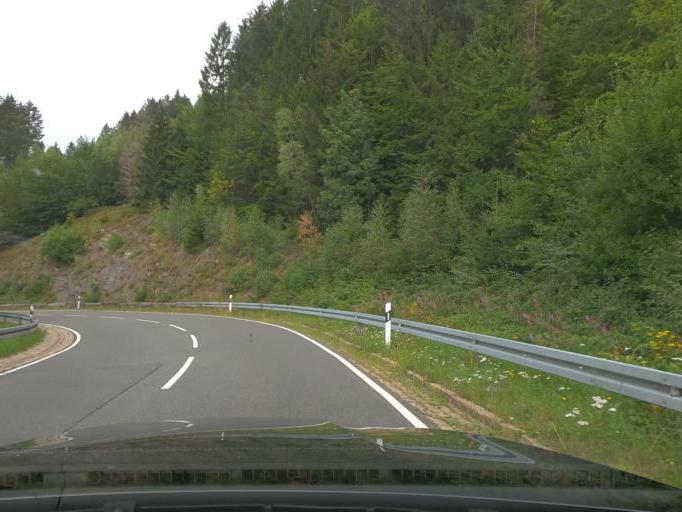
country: DE
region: Lower Saxony
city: Wildemann
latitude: 51.8628
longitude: 10.3119
